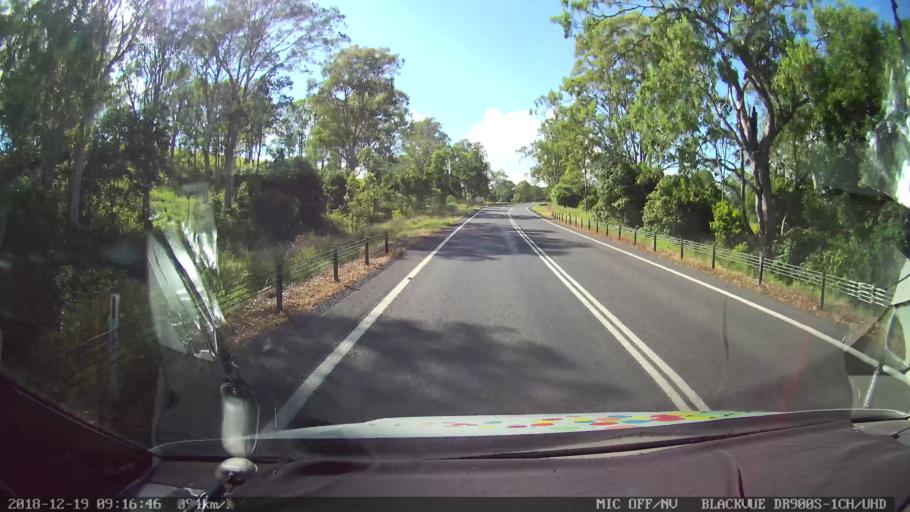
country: AU
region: New South Wales
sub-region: Kyogle
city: Kyogle
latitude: -28.5247
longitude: 152.9702
